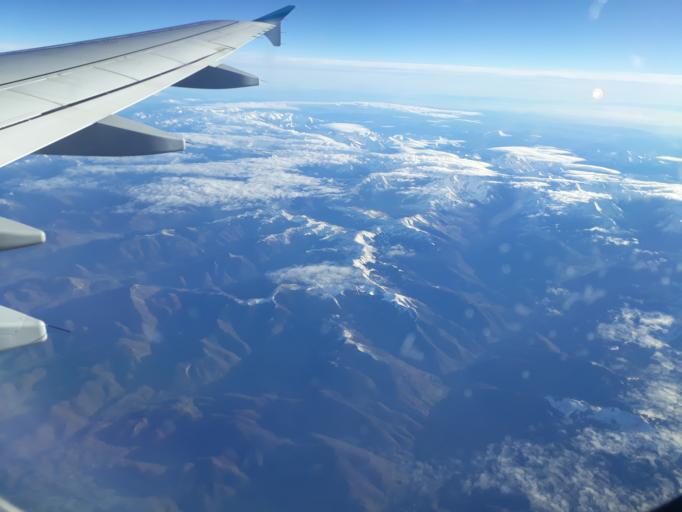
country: FR
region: Midi-Pyrenees
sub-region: Departement des Hautes-Pyrenees
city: Capvern
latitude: 43.1144
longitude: 0.3424
